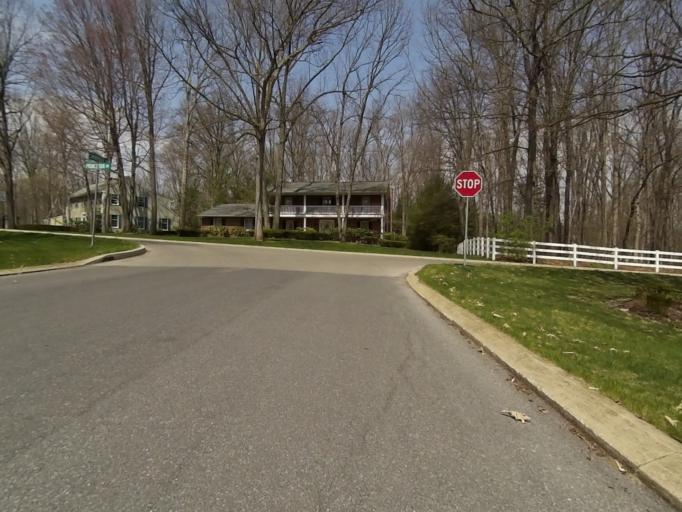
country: US
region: Pennsylvania
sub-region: Centre County
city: Park Forest Village
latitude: 40.7960
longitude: -77.9045
